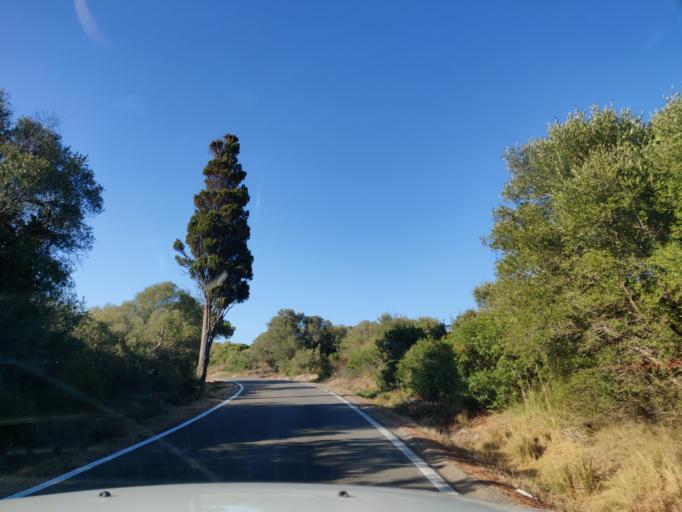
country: IT
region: Tuscany
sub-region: Provincia di Grosseto
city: Orbetello Scalo
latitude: 42.4151
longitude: 11.2990
